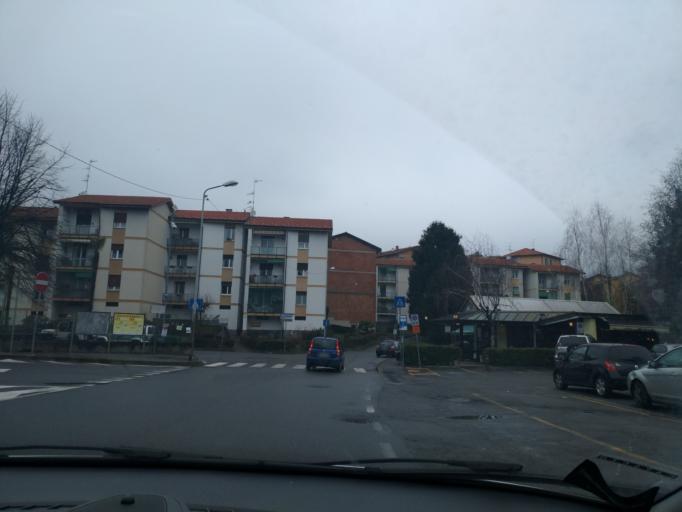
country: IT
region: Lombardy
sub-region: Provincia di Como
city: Maslianico
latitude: 45.8337
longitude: 9.0455
